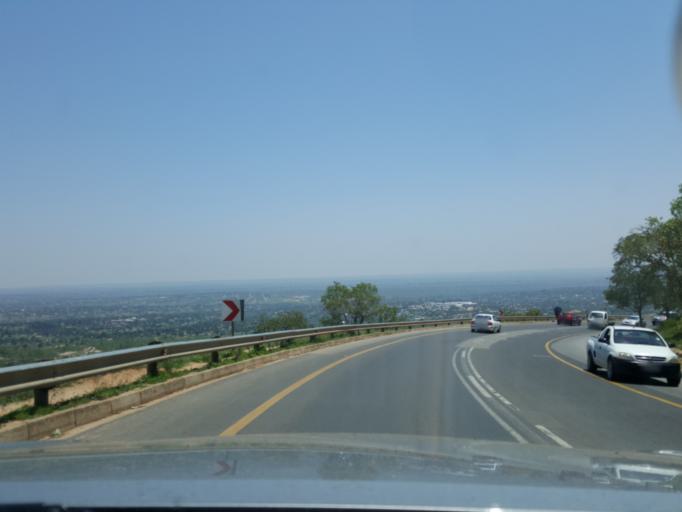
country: ZA
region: Limpopo
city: Thulamahashi
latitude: -24.8314
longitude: 31.0697
